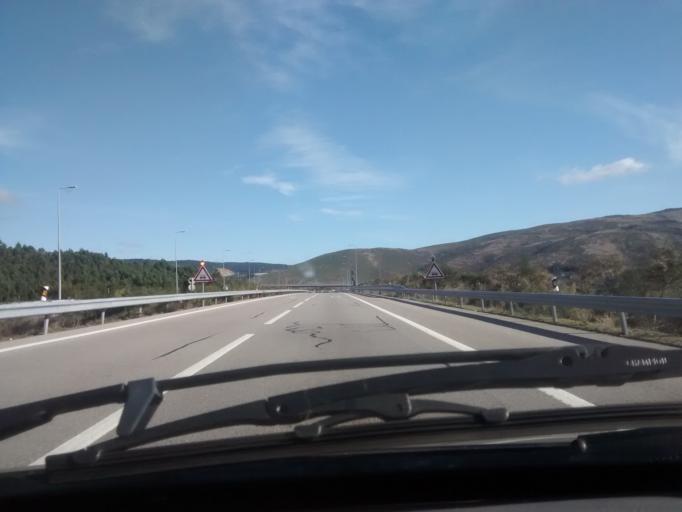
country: PT
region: Vila Real
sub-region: Ribeira de Pena
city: Ribeira de Pena
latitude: 41.4963
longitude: -7.8075
